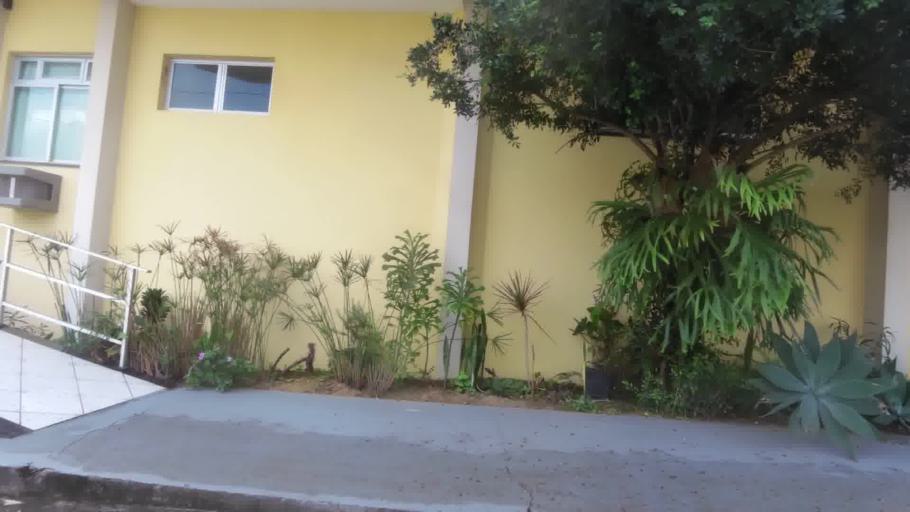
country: BR
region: Espirito Santo
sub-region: Piuma
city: Piuma
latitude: -20.8310
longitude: -40.6907
